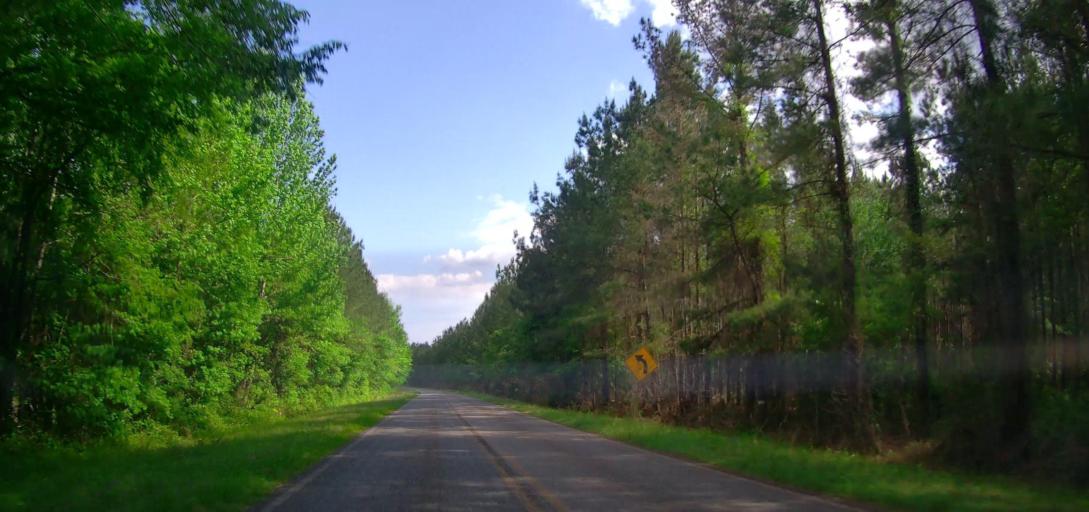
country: US
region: Georgia
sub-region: Laurens County
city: East Dublin
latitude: 32.7036
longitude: -82.9167
